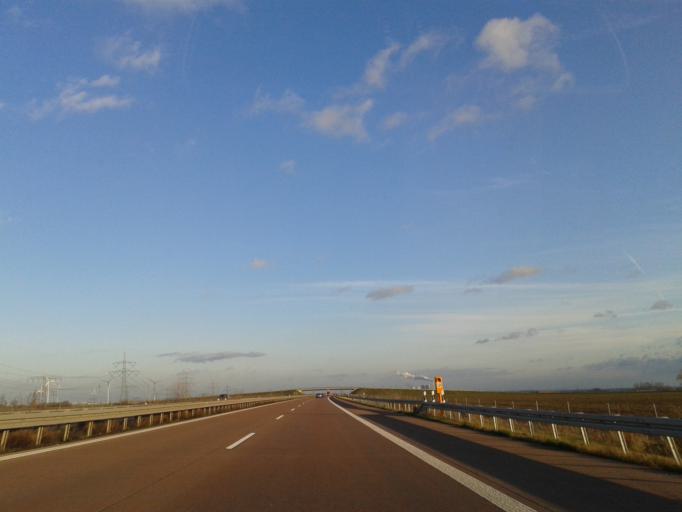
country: DE
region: Saxony-Anhalt
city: Schafstadt
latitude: 51.4046
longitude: 11.8139
